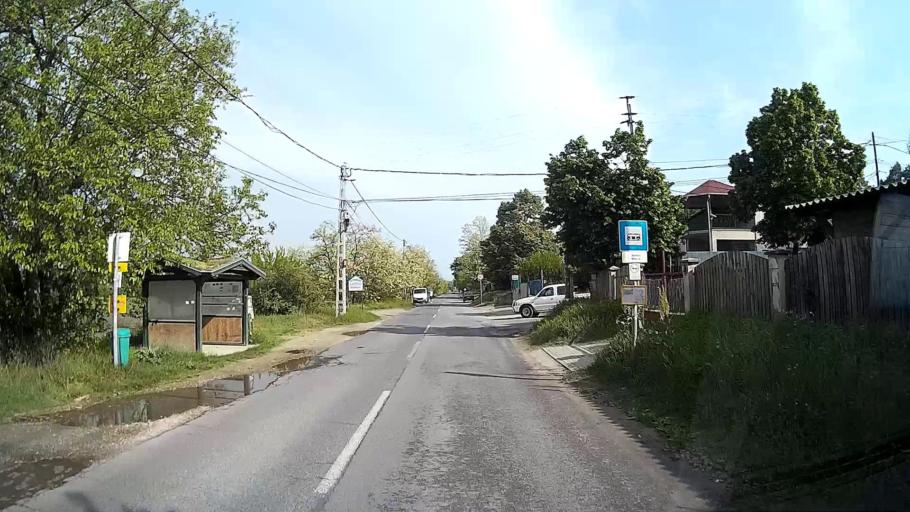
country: HU
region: Pest
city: Leanyfalu
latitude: 47.7139
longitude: 19.1057
